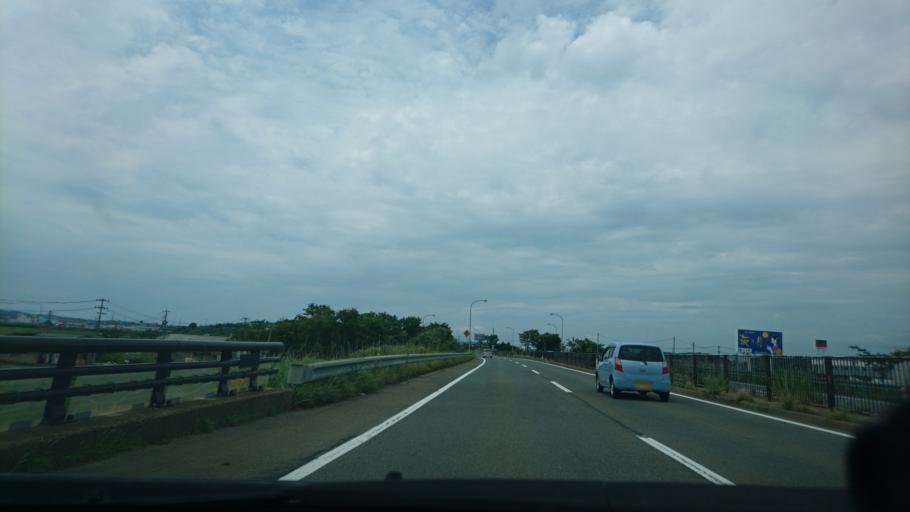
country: JP
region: Akita
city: Akita
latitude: 39.6753
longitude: 140.1512
